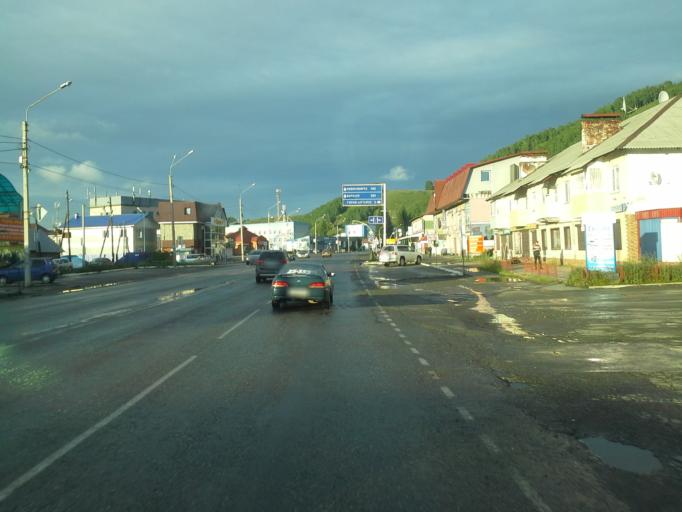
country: RU
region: Khabarovsk Krai
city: Mayma
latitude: 52.0034
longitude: 85.8993
